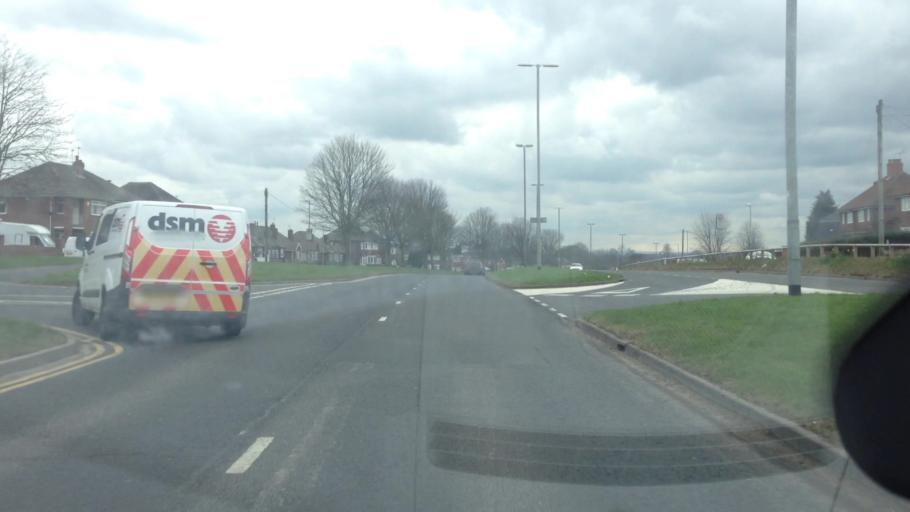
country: GB
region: England
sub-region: City and Borough of Leeds
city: Scholes
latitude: 53.8134
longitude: -1.4560
